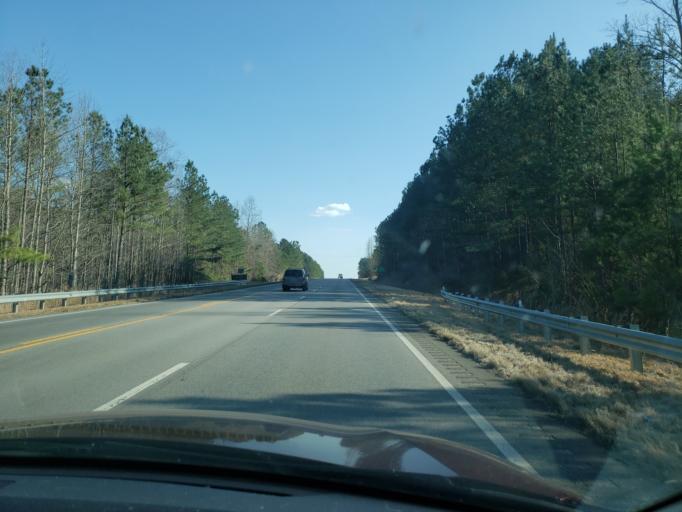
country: US
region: Alabama
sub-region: Cleburne County
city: Heflin
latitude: 33.4956
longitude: -85.5993
